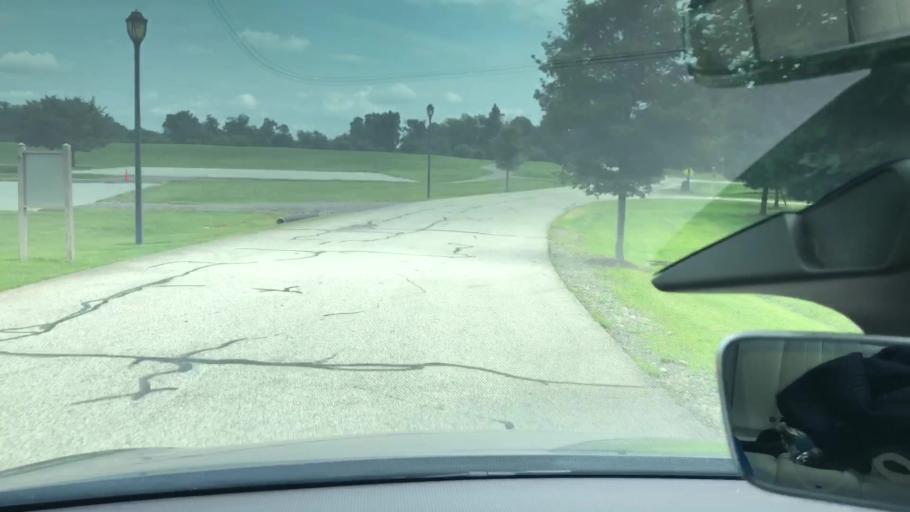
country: US
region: Pennsylvania
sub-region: Allegheny County
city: Pitcairn
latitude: 40.4194
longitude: -79.7684
